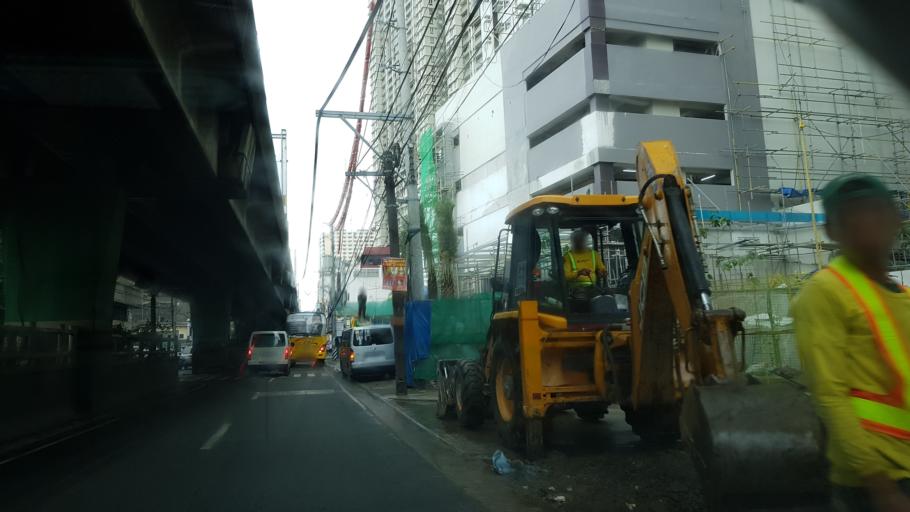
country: PH
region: Metro Manila
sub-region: Makati City
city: Makati City
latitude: 14.5584
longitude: 120.9966
